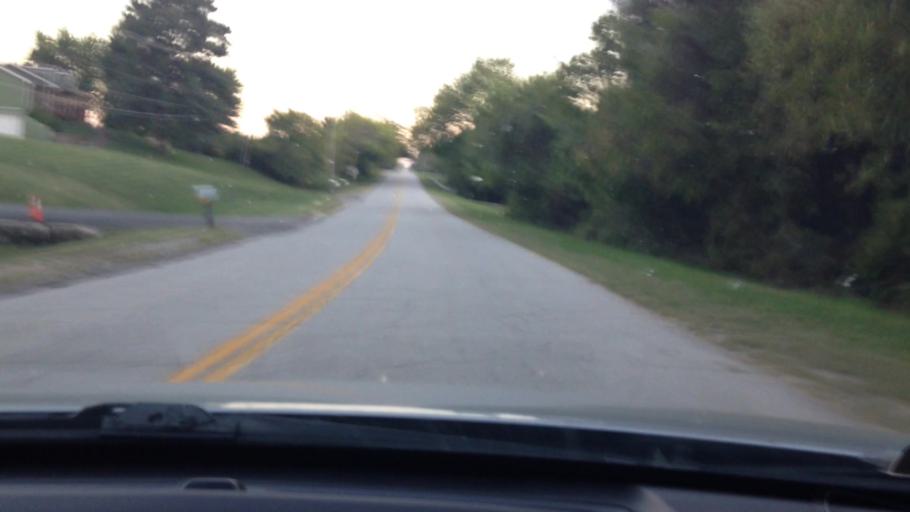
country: US
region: Kansas
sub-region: Leavenworth County
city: Lansing
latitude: 39.1838
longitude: -94.8267
